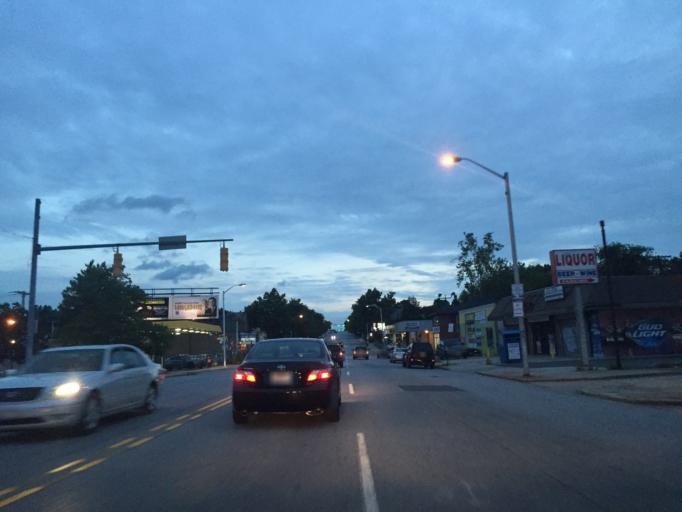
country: US
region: Maryland
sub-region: Baltimore County
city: Parkville
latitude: 39.3622
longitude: -76.5530
